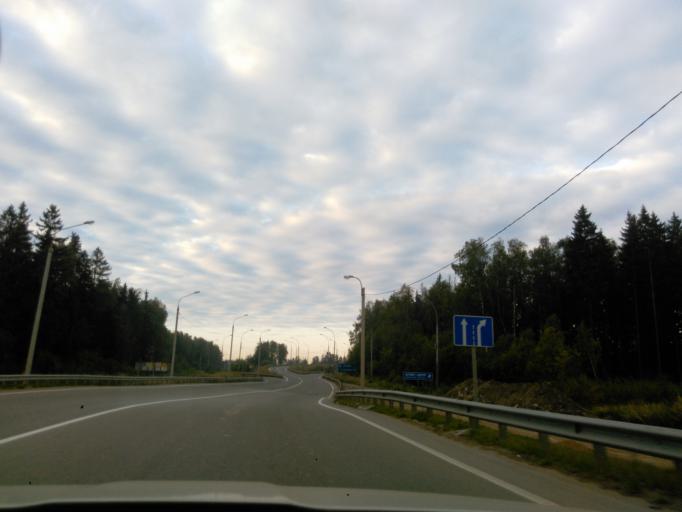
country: RU
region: Moskovskaya
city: Novopodrezkovo
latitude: 55.9710
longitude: 37.3287
